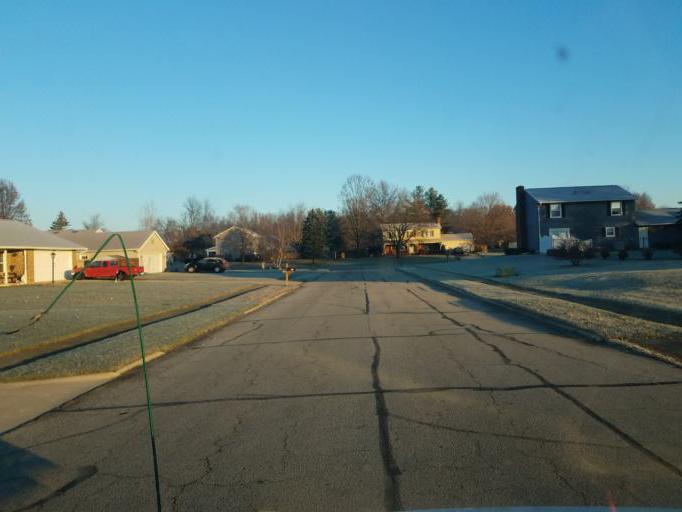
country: US
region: Ohio
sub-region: Marion County
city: Marion
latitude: 40.5689
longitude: -83.0965
